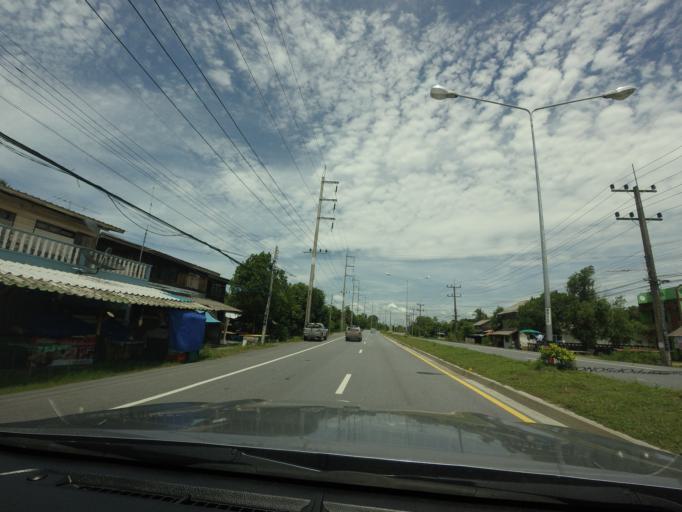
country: TH
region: Songkhla
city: Krasae Sin
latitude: 7.5704
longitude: 100.4101
